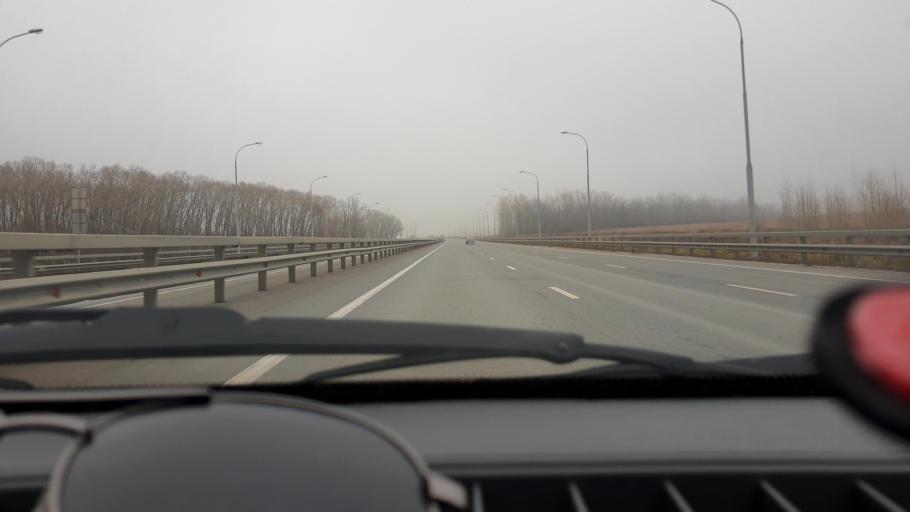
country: RU
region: Bashkortostan
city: Kabakovo
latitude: 54.6514
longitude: 56.0954
